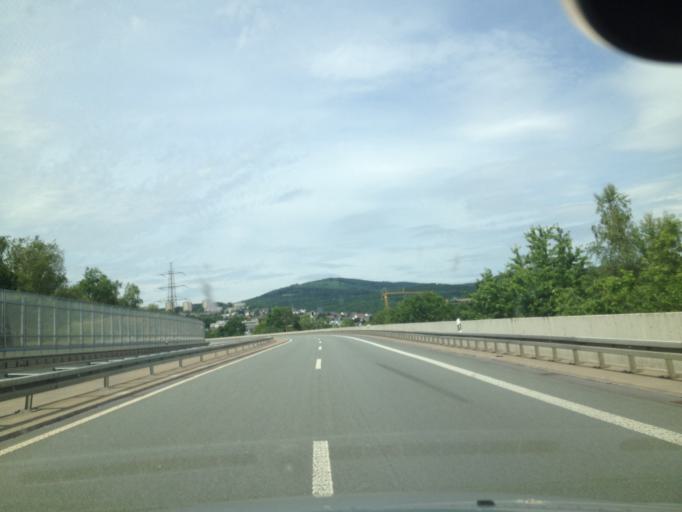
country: DE
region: North Rhine-Westphalia
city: Kreuztal
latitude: 50.9541
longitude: 7.9897
